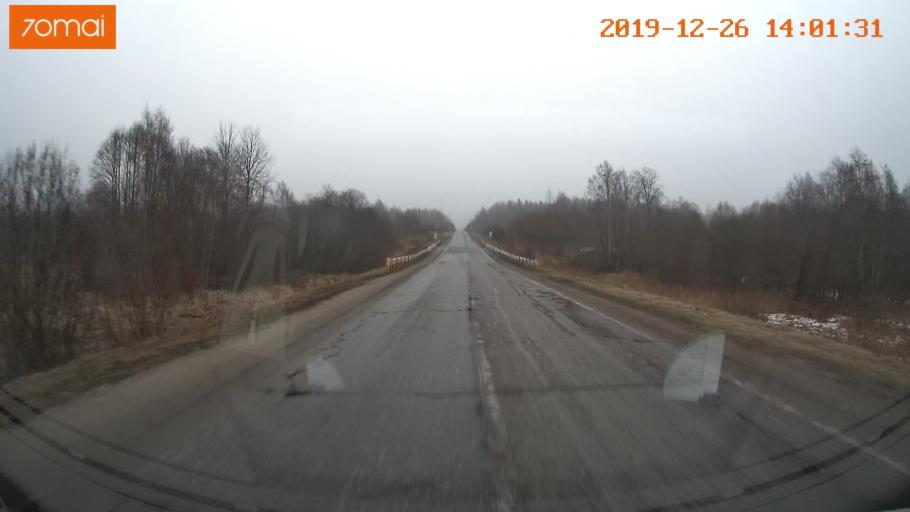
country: RU
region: Jaroslavl
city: Poshekhon'ye
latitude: 58.5499
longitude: 38.7653
